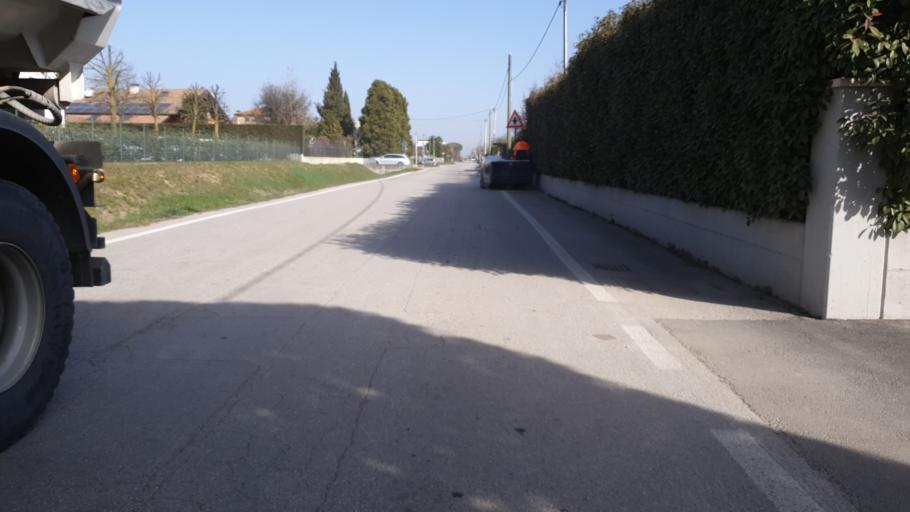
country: IT
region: Veneto
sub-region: Provincia di Padova
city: Mejaniga
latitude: 45.4757
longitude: 11.9162
